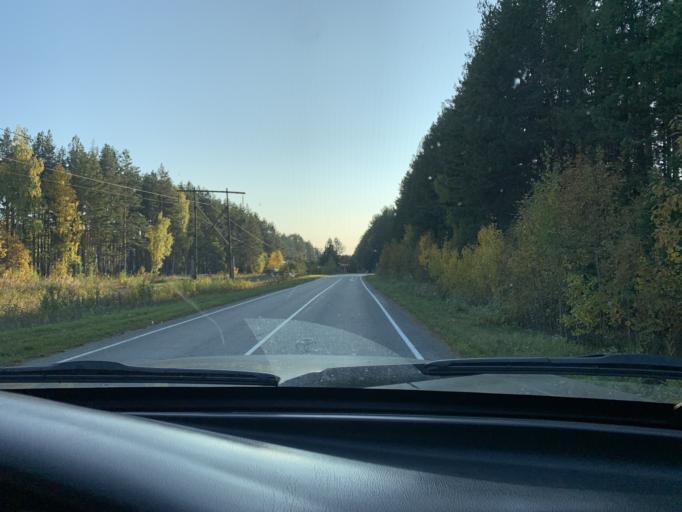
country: RU
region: Sverdlovsk
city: Verkhneye Dubrovo
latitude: 56.8658
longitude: 61.0908
